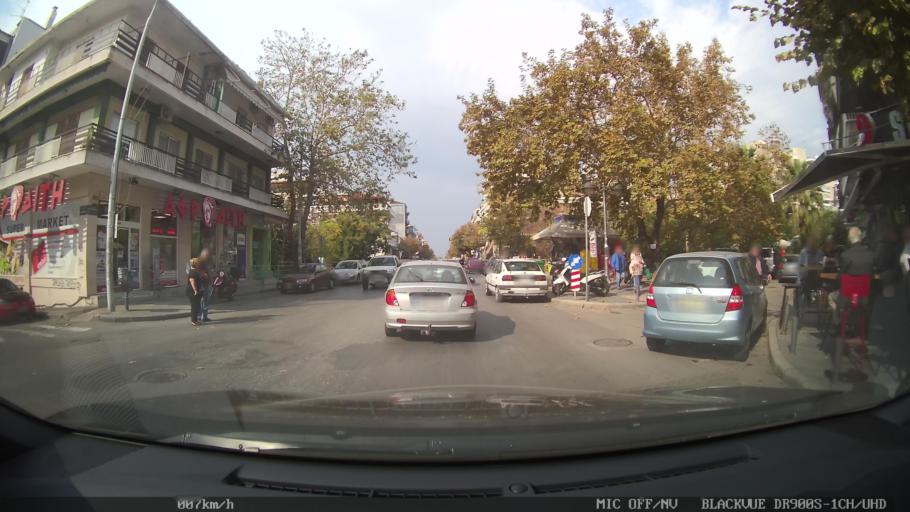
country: GR
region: Central Macedonia
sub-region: Nomos Thessalonikis
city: Triandria
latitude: 40.6143
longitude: 22.9788
